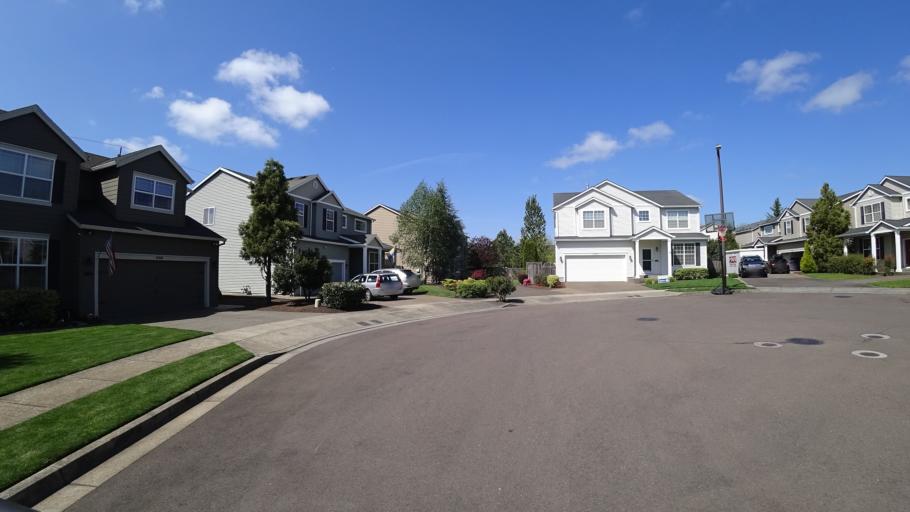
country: US
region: Oregon
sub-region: Washington County
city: King City
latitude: 45.4272
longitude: -122.8413
